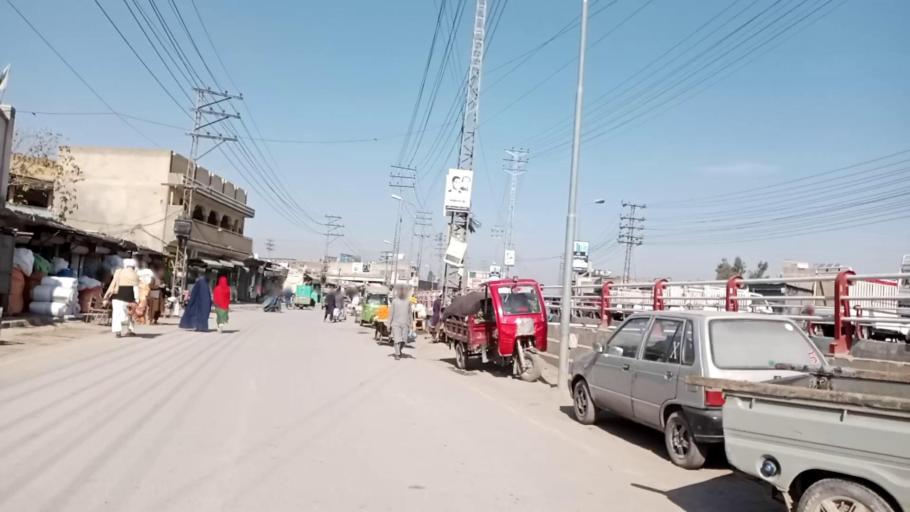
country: PK
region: Khyber Pakhtunkhwa
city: Peshawar
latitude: 33.9943
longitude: 71.4708
